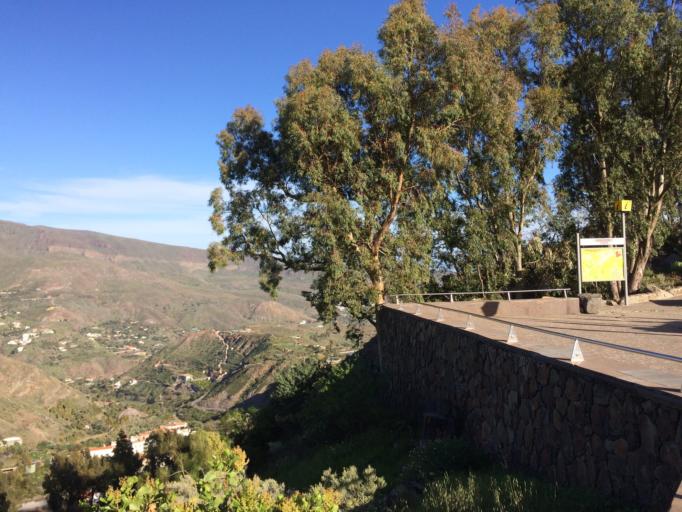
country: ES
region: Canary Islands
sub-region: Provincia de Las Palmas
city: San Bartolome
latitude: 27.9212
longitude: -15.5745
